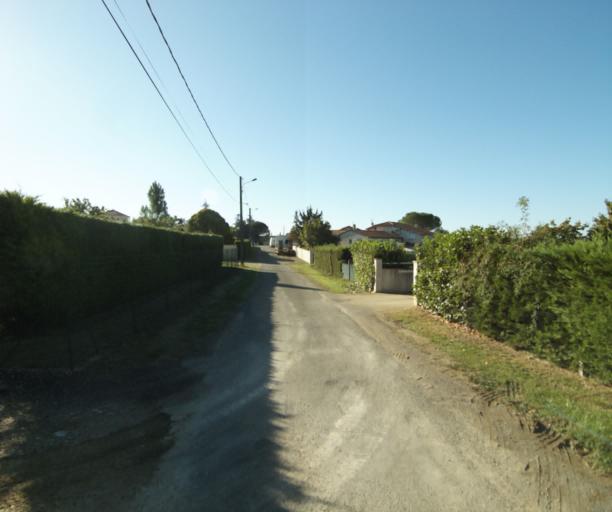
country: FR
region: Midi-Pyrenees
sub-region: Departement du Gers
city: Gondrin
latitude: 43.8407
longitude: 0.2536
